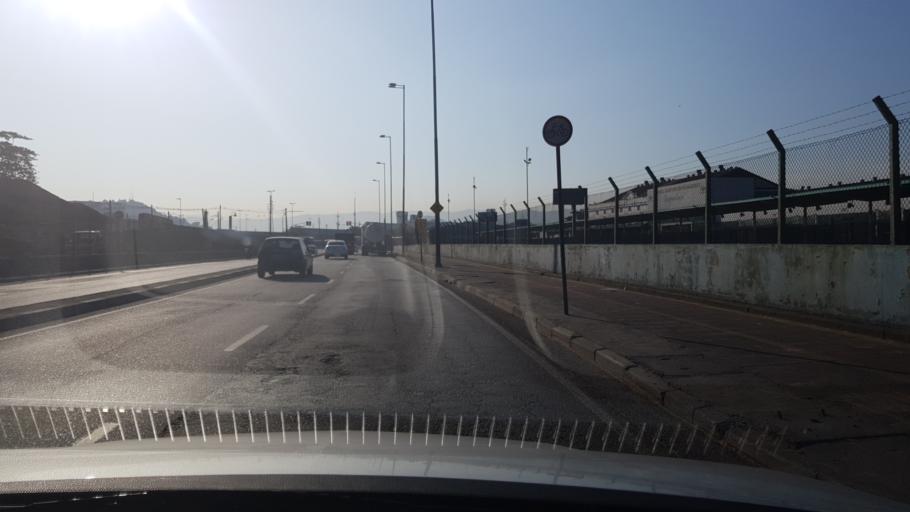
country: BR
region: Sao Paulo
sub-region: Santos
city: Santos
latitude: -23.9539
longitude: -46.3105
